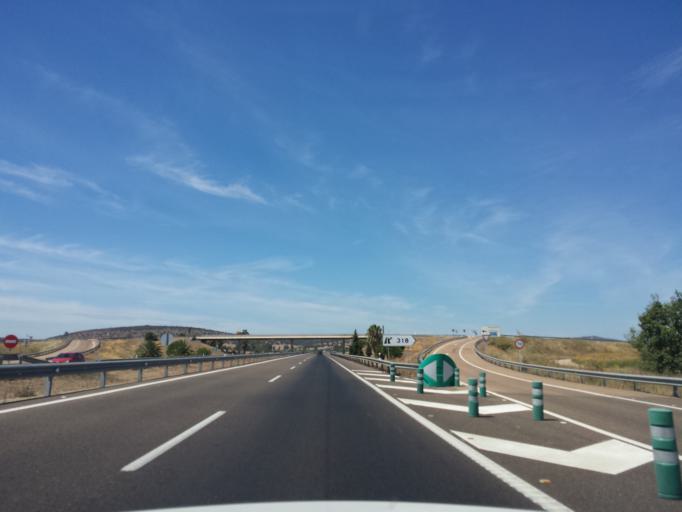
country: ES
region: Extremadura
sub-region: Provincia de Badajoz
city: San Pedro de Merida
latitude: 38.9902
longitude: -6.1189
